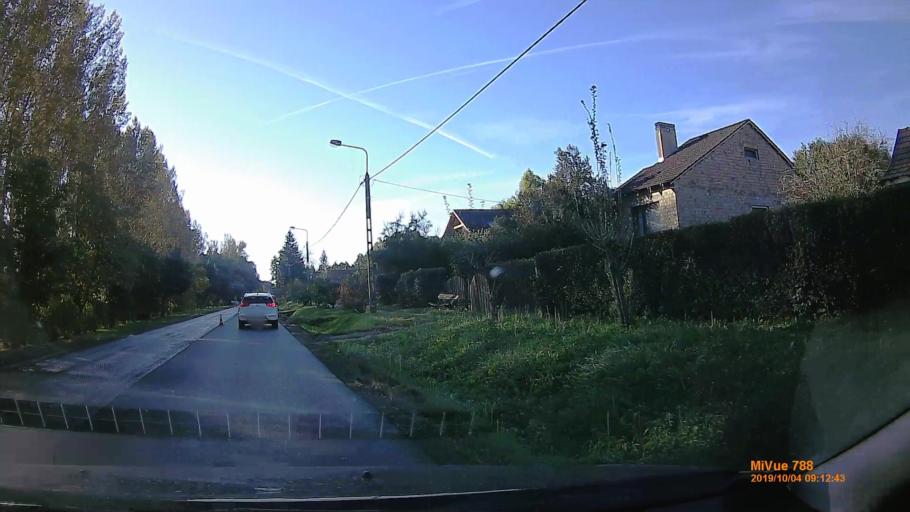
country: HU
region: Somogy
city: Karad
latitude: 46.6539
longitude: 17.7843
